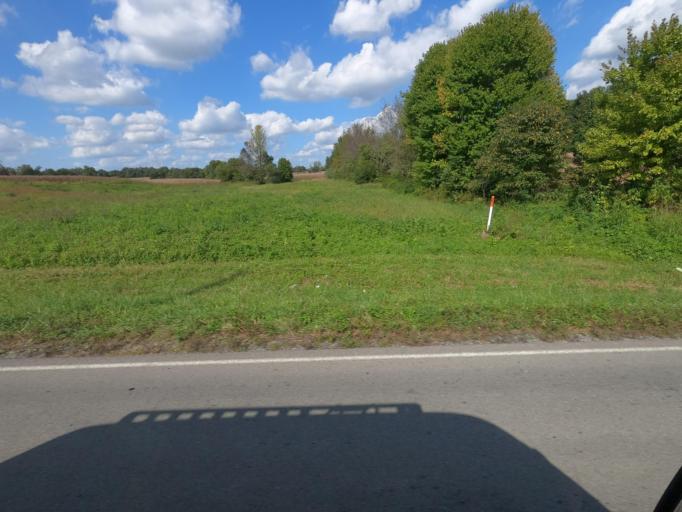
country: US
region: Illinois
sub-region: Massac County
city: Metropolis
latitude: 37.1912
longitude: -88.6927
